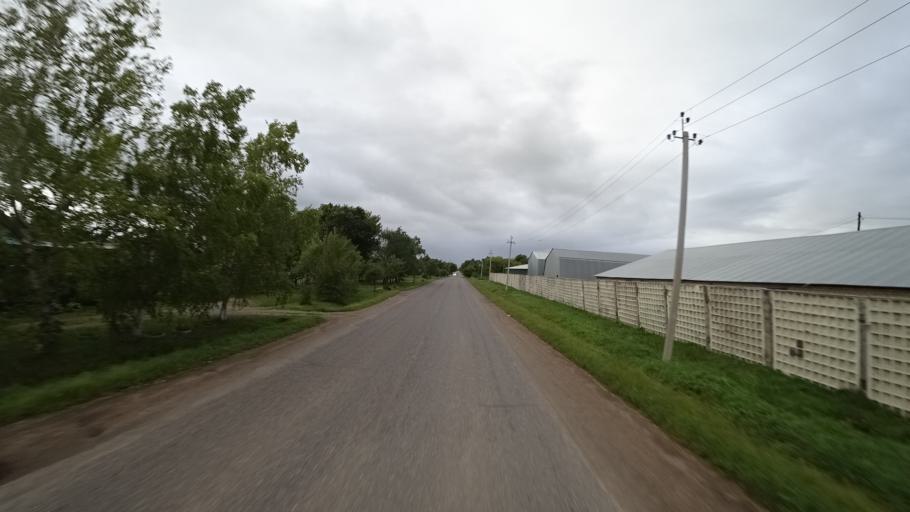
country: RU
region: Primorskiy
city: Chernigovka
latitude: 44.3362
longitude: 132.5902
